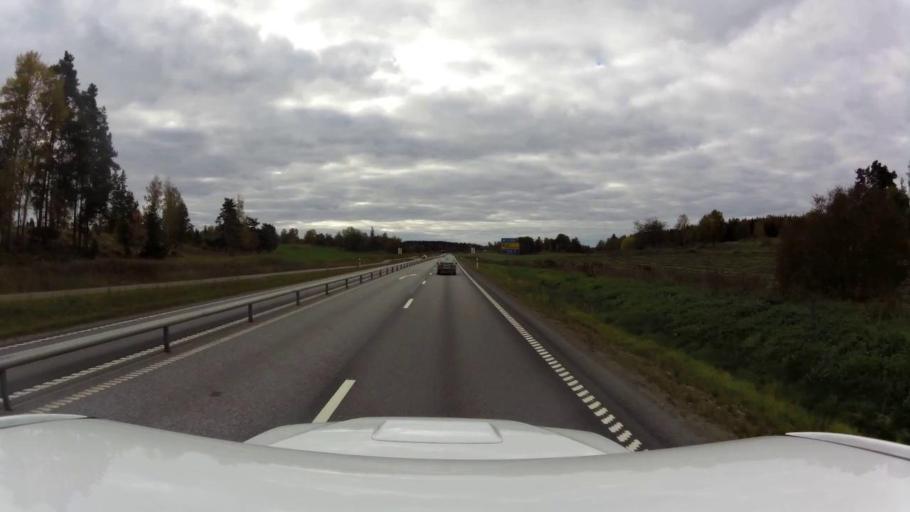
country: SE
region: OEstergoetland
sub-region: Linkopings Kommun
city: Malmslatt
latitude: 58.3174
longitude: 15.5675
